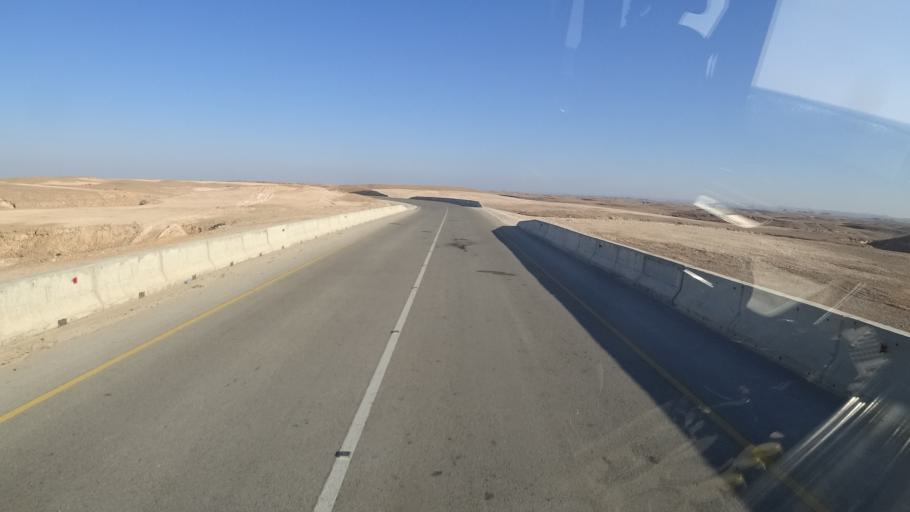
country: YE
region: Al Mahrah
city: Hawf
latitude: 17.0789
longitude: 53.0183
